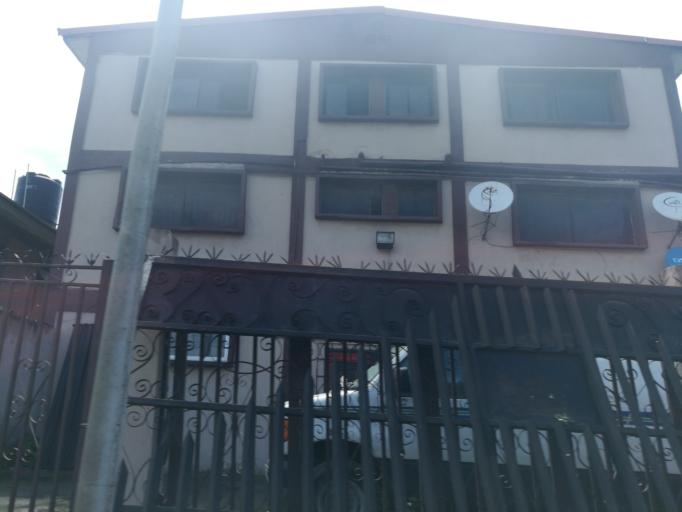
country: NG
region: Lagos
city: Ojota
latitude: 6.5630
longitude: 3.3688
